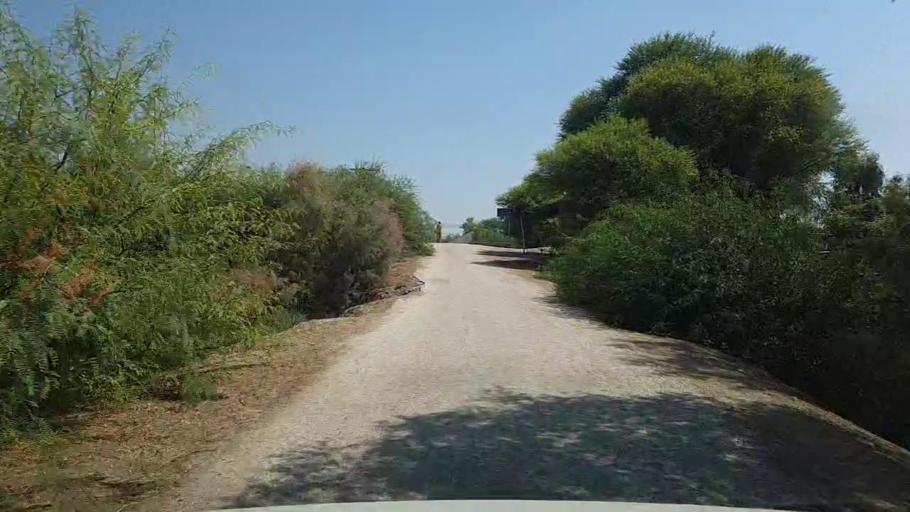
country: PK
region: Sindh
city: Kandhkot
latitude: 28.2884
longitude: 69.3534
